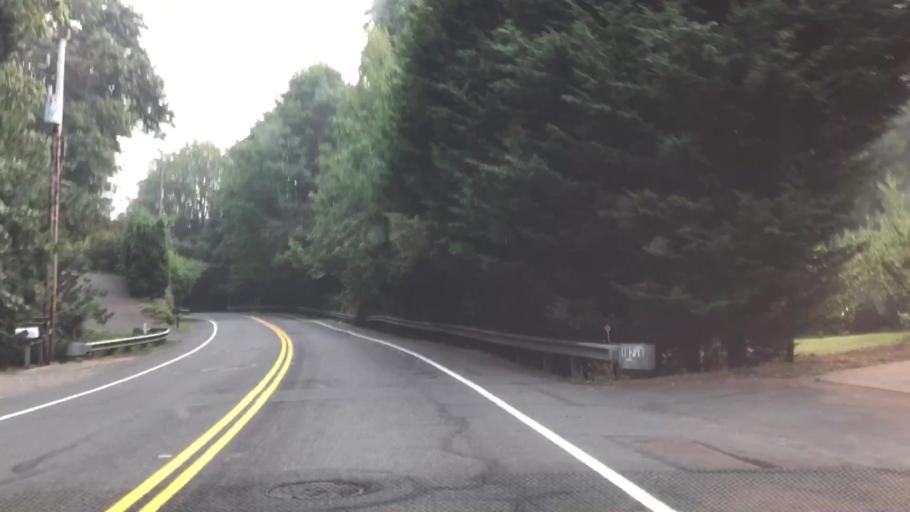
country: US
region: Washington
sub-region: King County
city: Lake Forest Park
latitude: 47.7723
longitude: -122.2921
